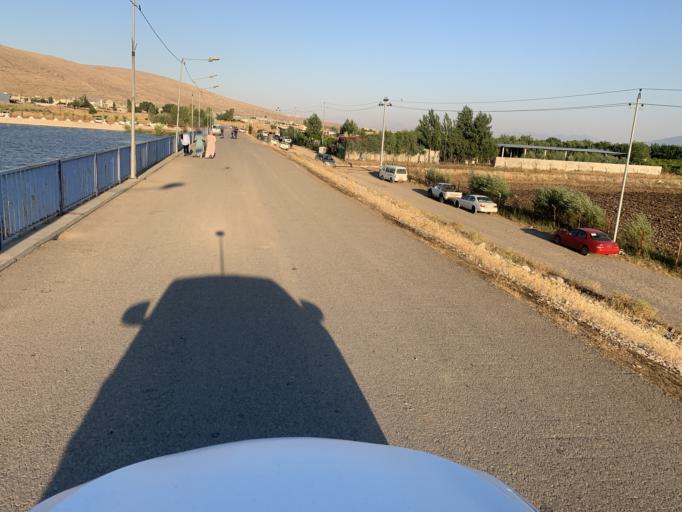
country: IQ
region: As Sulaymaniyah
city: Raniye
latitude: 36.2721
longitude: 44.7531
